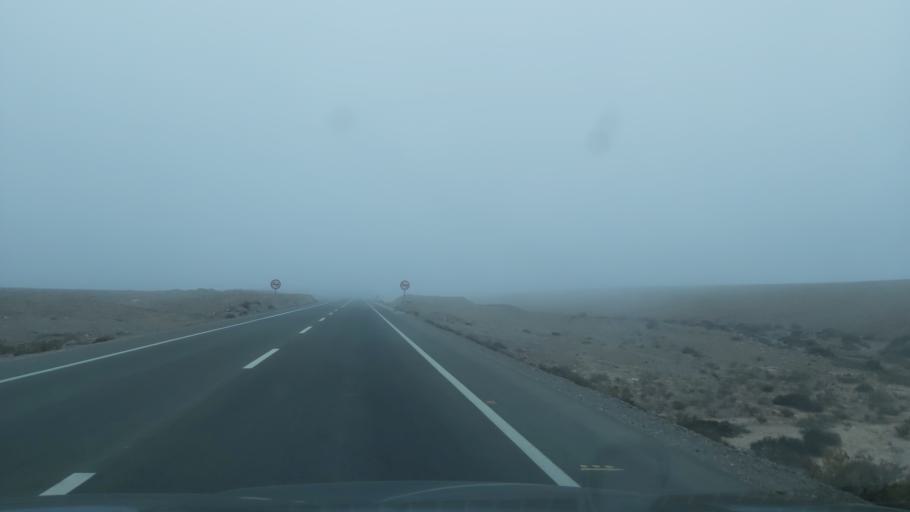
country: CL
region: Atacama
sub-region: Provincia de Copiapo
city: Copiapo
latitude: -27.2813
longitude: -70.0916
